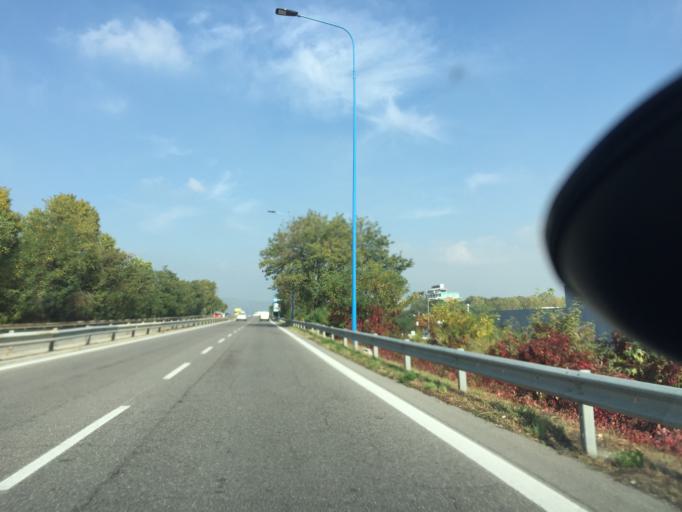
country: IT
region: Lombardy
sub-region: Provincia di Brescia
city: Roncadelle
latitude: 45.5198
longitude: 10.1723
